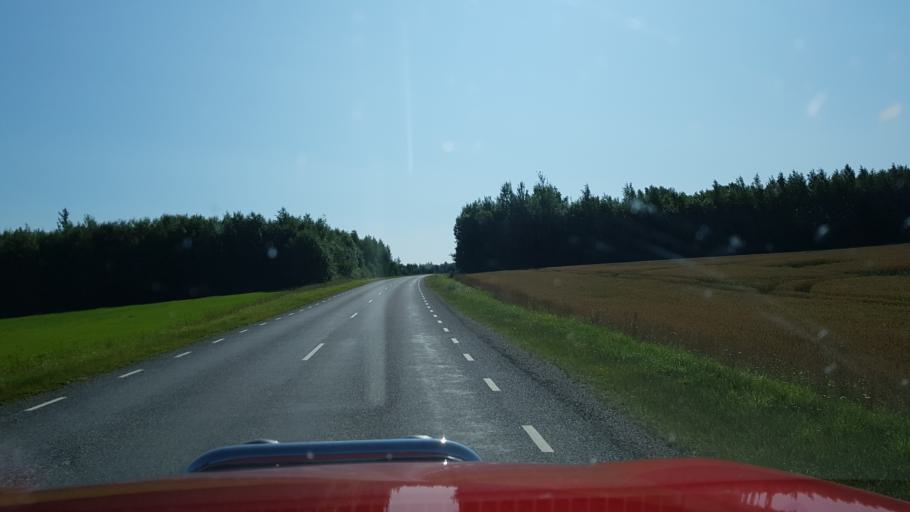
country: EE
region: Vorumaa
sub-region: Voru linn
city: Voru
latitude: 57.9767
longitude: 26.8148
